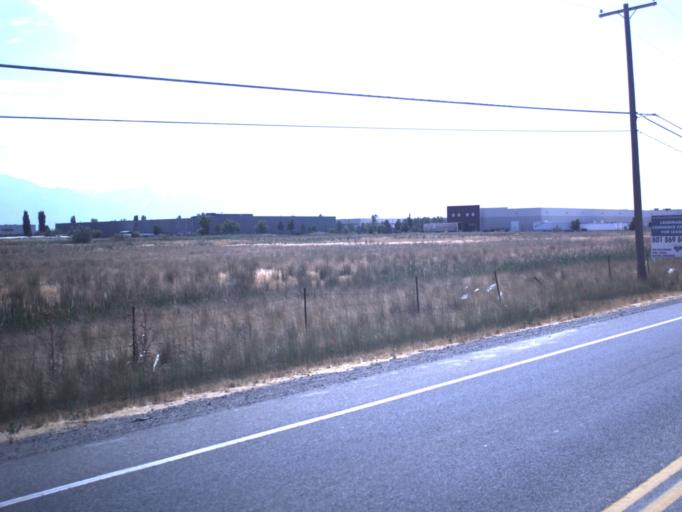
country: US
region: Utah
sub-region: Salt Lake County
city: West Valley City
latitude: 40.7371
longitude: -112.0249
